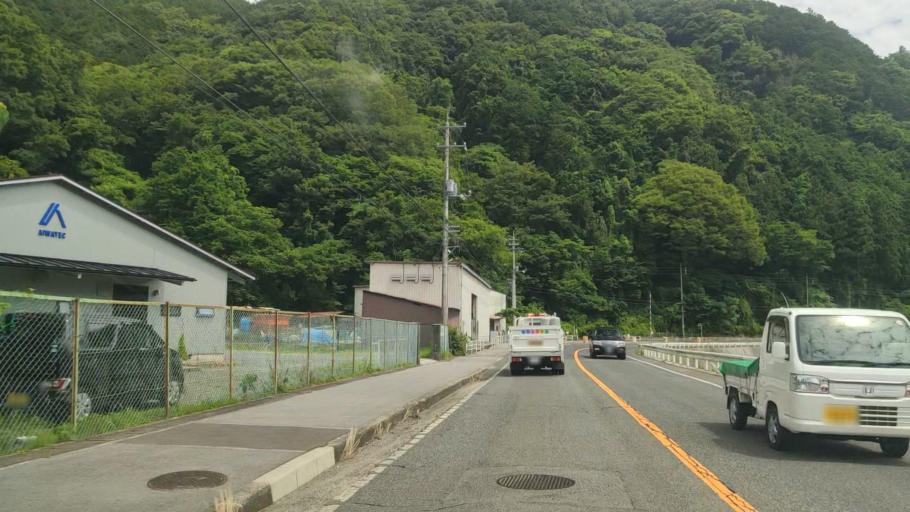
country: JP
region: Okayama
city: Niimi
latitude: 35.0736
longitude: 133.6805
